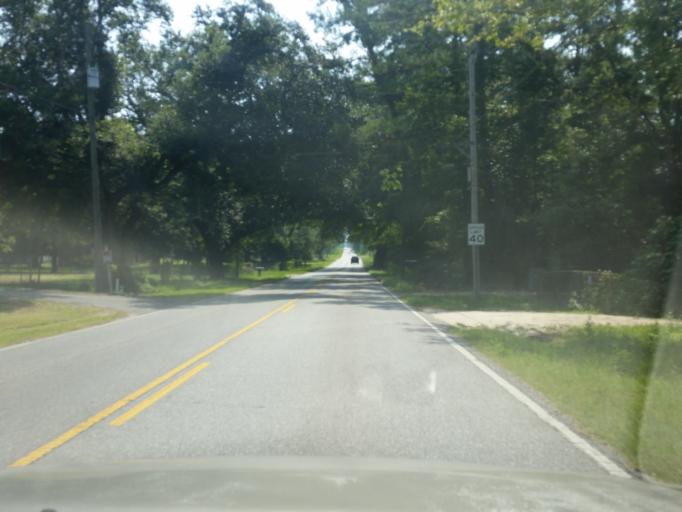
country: US
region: Florida
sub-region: Escambia County
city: Ensley
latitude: 30.5193
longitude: -87.2992
